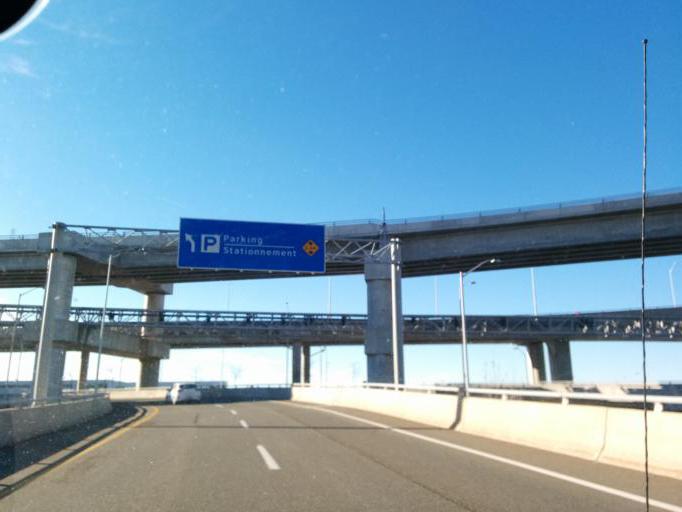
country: CA
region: Ontario
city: Etobicoke
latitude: 43.6851
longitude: -79.6151
